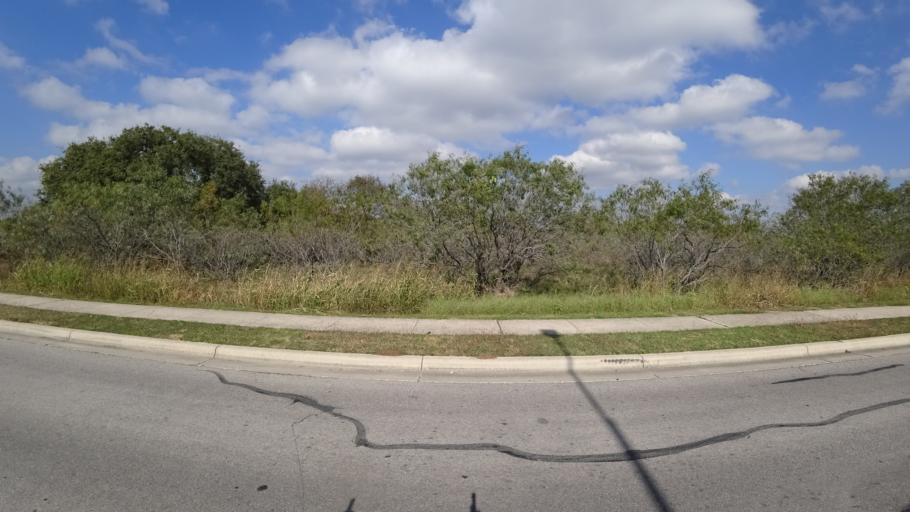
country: US
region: Texas
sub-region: Travis County
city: Shady Hollow
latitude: 30.1599
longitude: -97.8452
